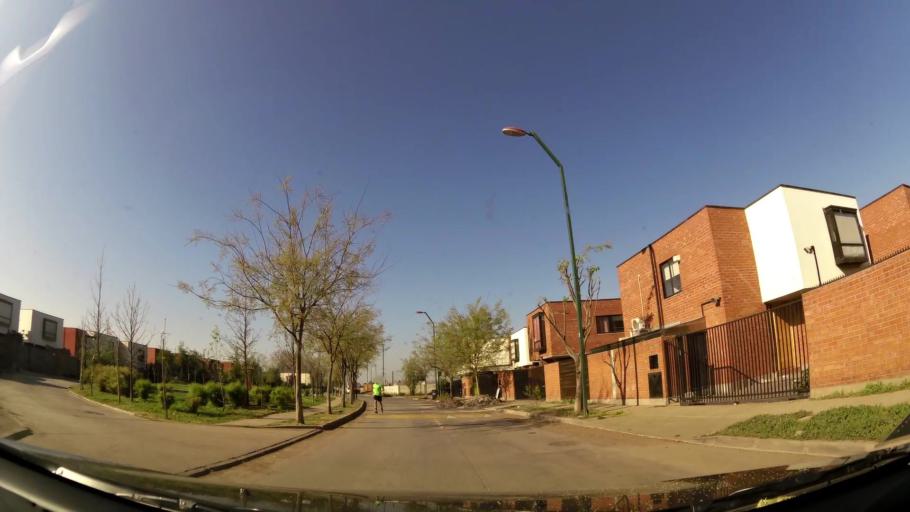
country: CL
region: Santiago Metropolitan
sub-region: Provincia de Chacabuco
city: Chicureo Abajo
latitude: -33.3659
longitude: -70.6677
